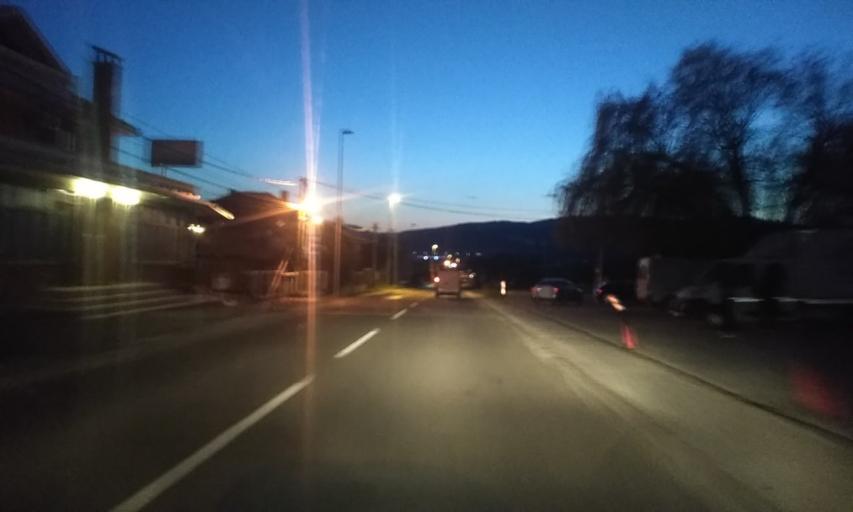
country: RS
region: Central Serbia
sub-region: Pcinjski Okrug
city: Vladicin Han
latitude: 42.7103
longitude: 22.1078
